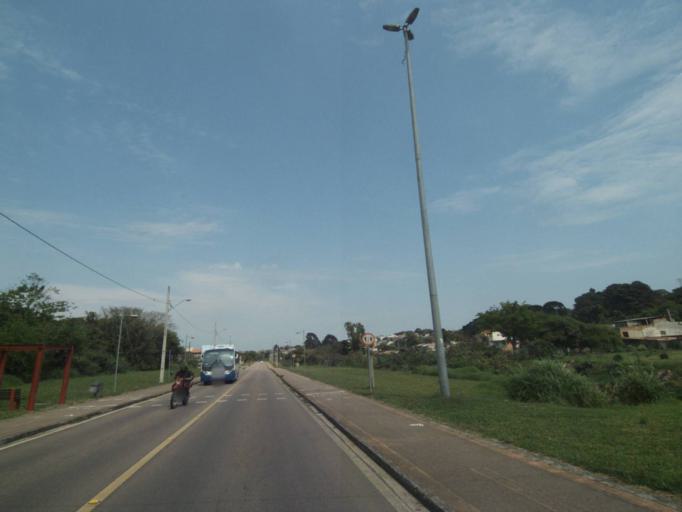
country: BR
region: Parana
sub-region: Curitiba
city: Curitiba
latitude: -25.4721
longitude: -49.3244
